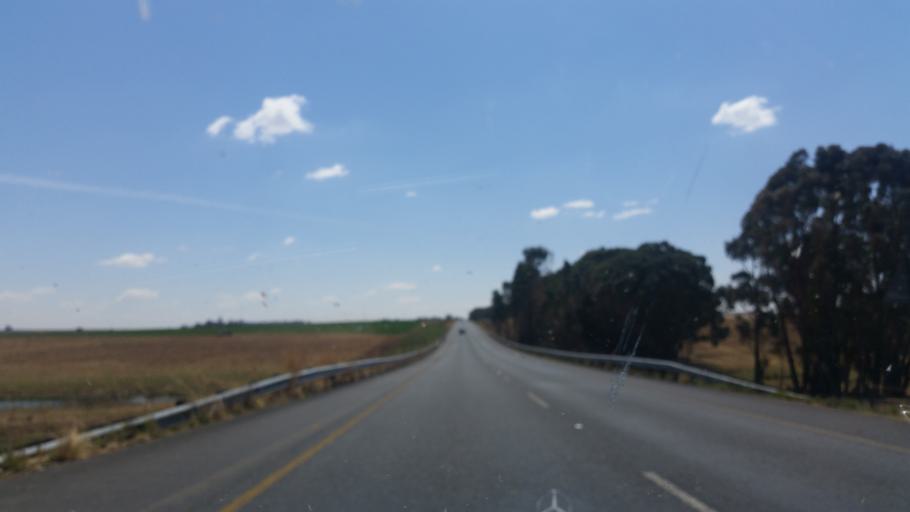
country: ZA
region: Orange Free State
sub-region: Thabo Mofutsanyana District Municipality
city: Bethlehem
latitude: -28.1004
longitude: 28.6581
